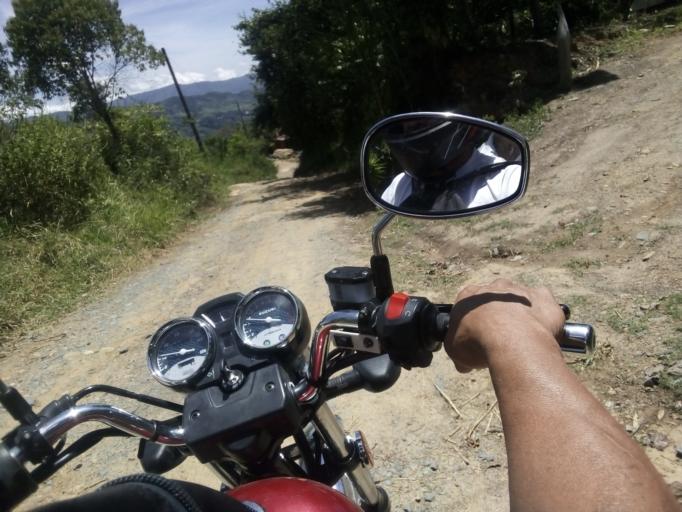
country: CO
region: Santander
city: Guepsa
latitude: 6.0109
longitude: -73.5554
